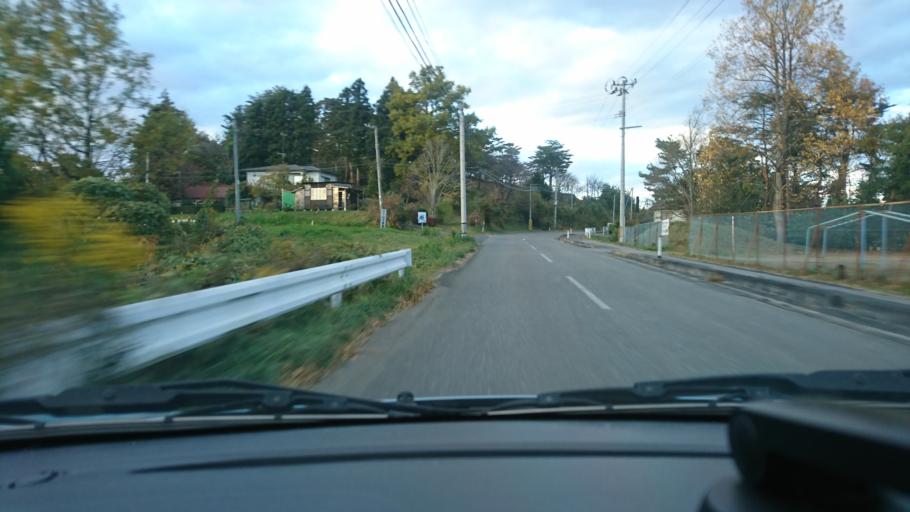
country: JP
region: Iwate
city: Ichinoseki
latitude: 38.7973
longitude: 141.1927
